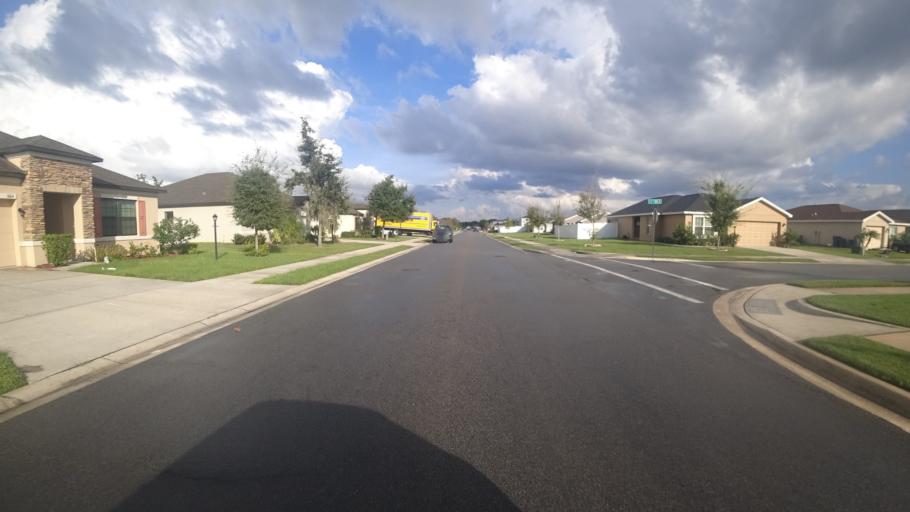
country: US
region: Florida
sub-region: Manatee County
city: Memphis
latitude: 27.5353
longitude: -82.5533
